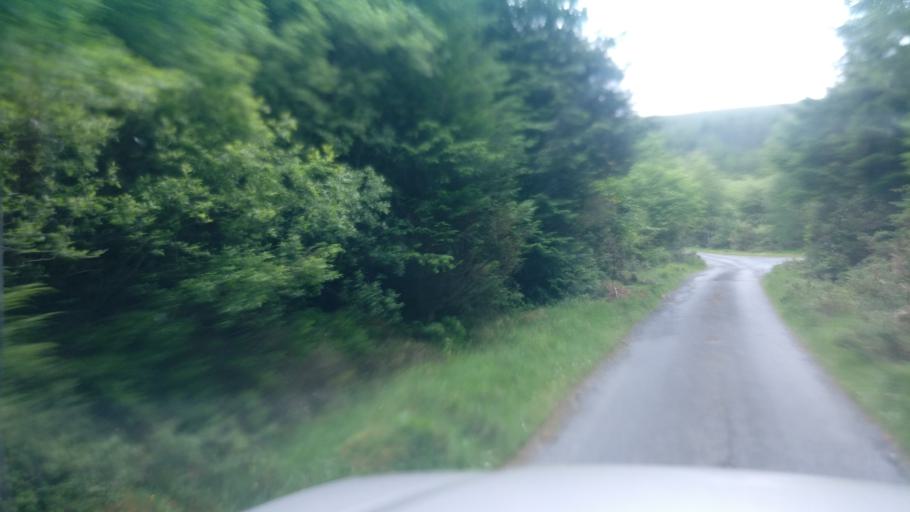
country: IE
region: Connaught
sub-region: County Galway
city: Loughrea
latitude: 53.1139
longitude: -8.6751
